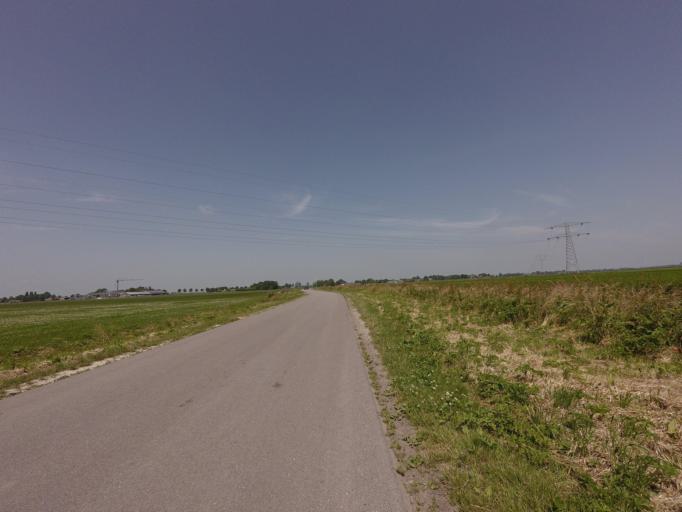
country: NL
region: North Holland
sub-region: Gemeente Opmeer
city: Opmeer
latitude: 52.6421
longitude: 4.9574
